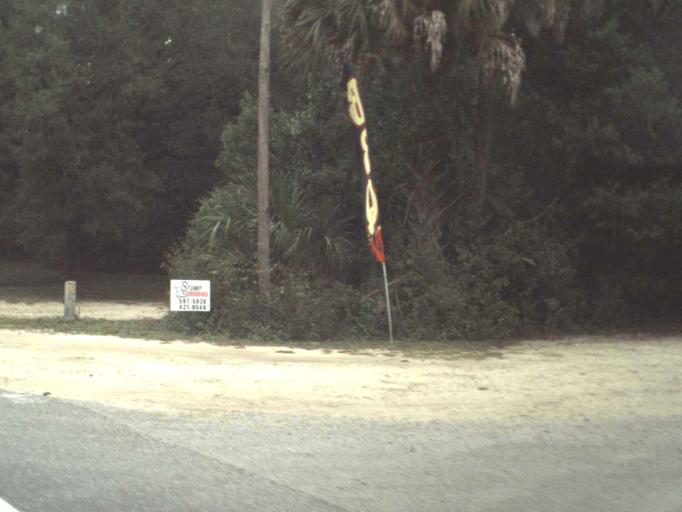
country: US
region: Florida
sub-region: Wakulla County
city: Crawfordville
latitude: 30.0926
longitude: -84.3855
